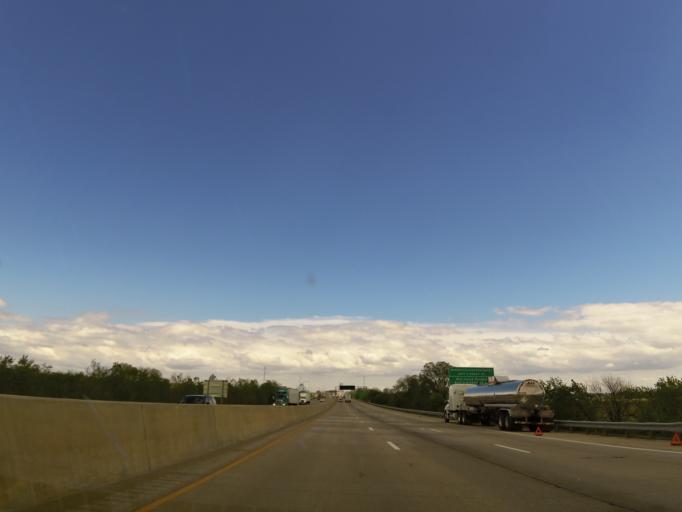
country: US
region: Tennessee
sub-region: Shelby County
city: Memphis
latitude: 35.1530
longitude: -90.0962
